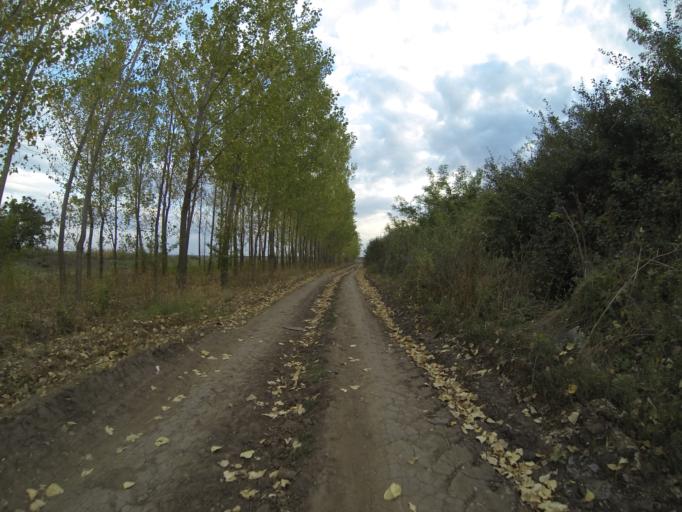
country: RO
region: Dolj
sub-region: Comuna Ceratu
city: Ceratu
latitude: 44.1064
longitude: 23.6936
